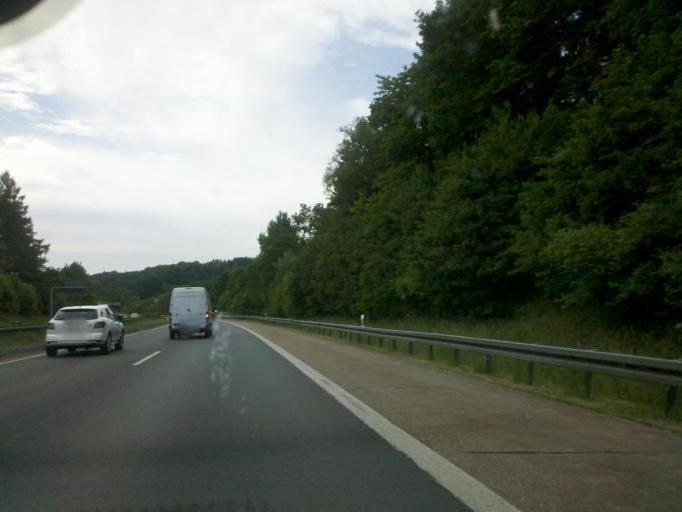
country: DE
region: North Rhine-Westphalia
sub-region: Regierungsbezirk Arnsberg
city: Luedenscheid
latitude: 51.2405
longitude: 7.6438
